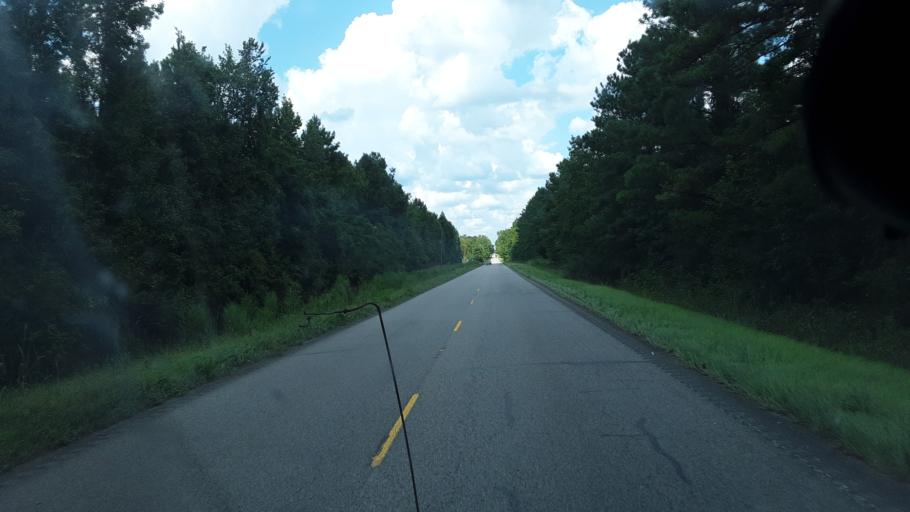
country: US
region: South Carolina
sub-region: Williamsburg County
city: Andrews
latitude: 33.5818
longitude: -79.4474
